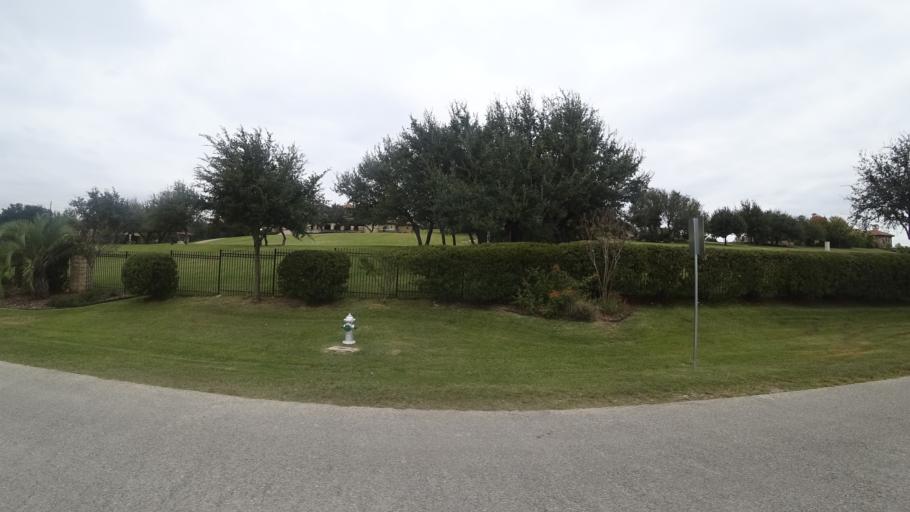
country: US
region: Texas
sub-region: Travis County
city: Lakeway
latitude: 30.3705
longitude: -97.9427
